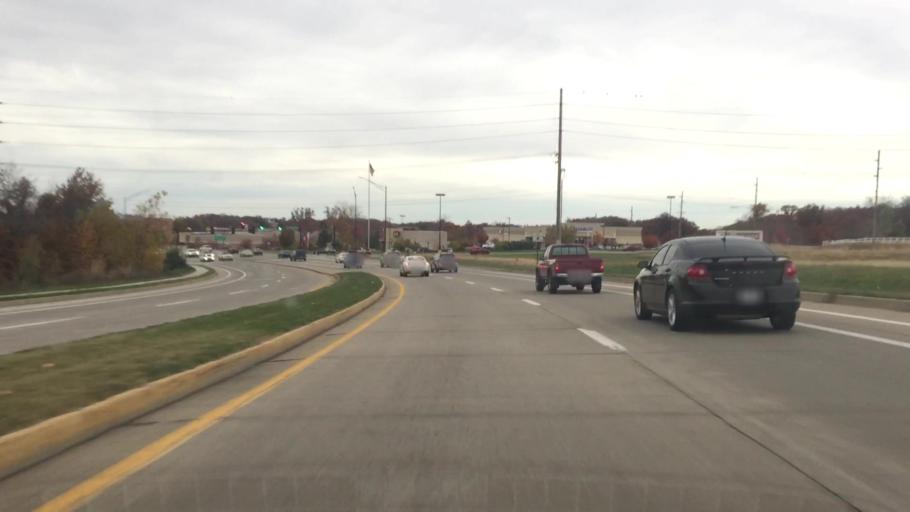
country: US
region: Missouri
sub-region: Boone County
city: Columbia
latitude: 38.9136
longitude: -92.3169
